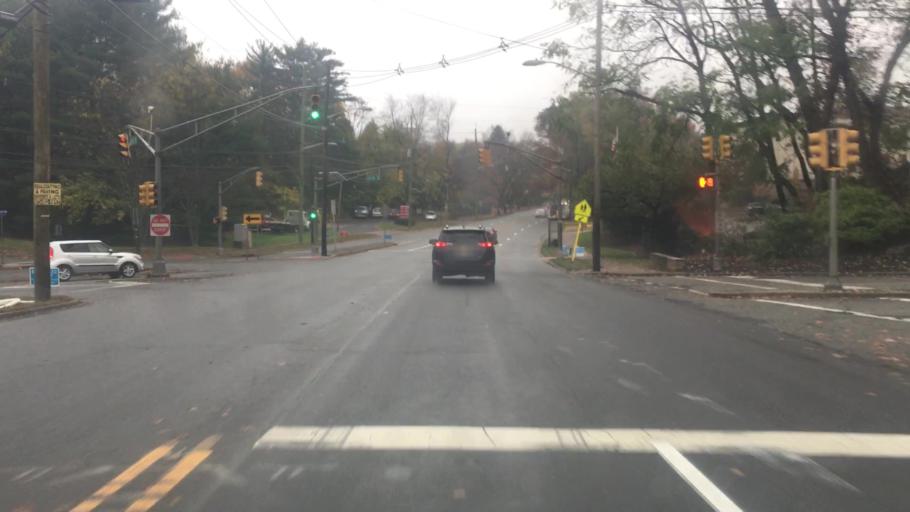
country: US
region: New Jersey
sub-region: Bergen County
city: Oakland
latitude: 40.9723
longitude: -74.2637
